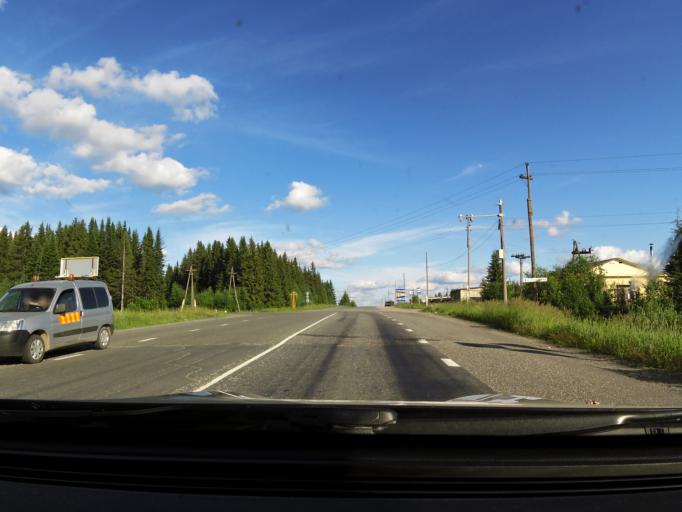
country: RU
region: Kirov
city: Omutninsk
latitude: 58.6839
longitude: 52.1425
